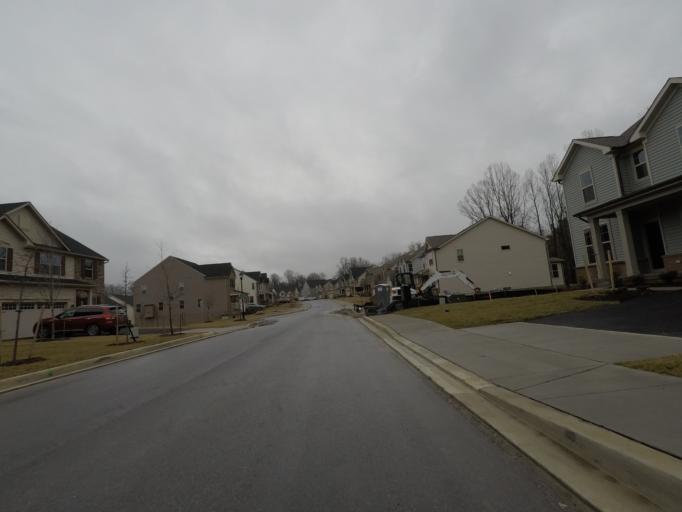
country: US
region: Maryland
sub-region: Howard County
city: Ellicott City
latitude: 39.3068
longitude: -76.8205
